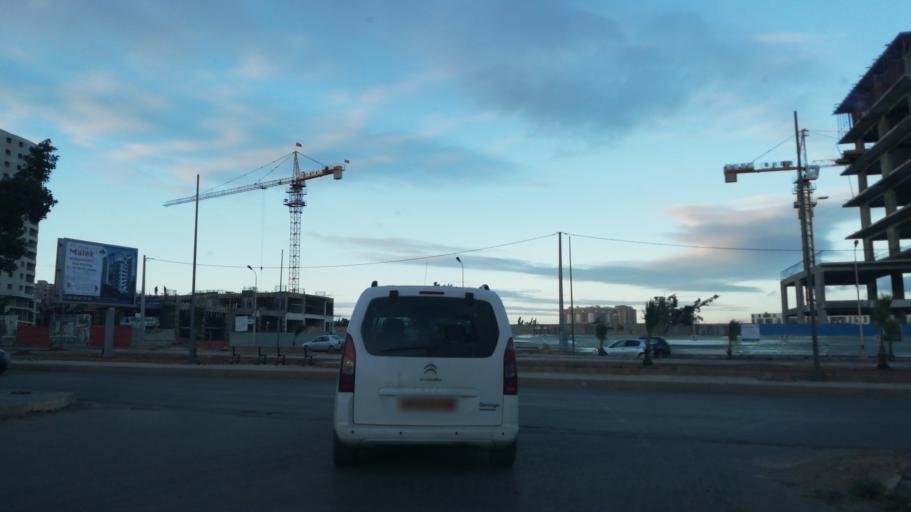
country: DZ
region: Oran
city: Bir el Djir
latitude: 35.7069
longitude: -0.5601
